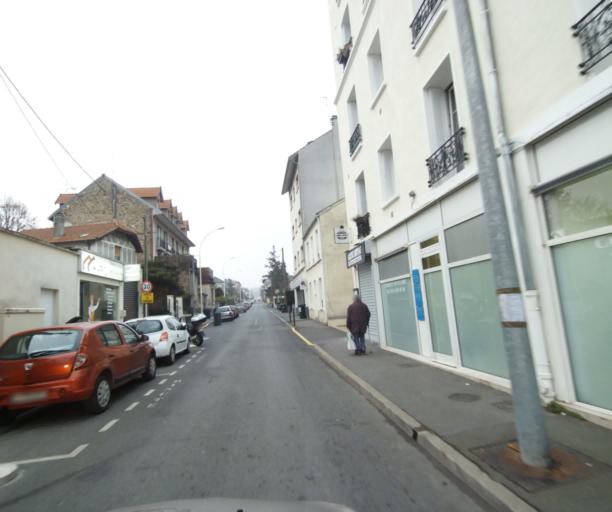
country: FR
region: Ile-de-France
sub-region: Departement de Seine-Saint-Denis
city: Neuilly-Plaisance
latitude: 48.8626
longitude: 2.5045
